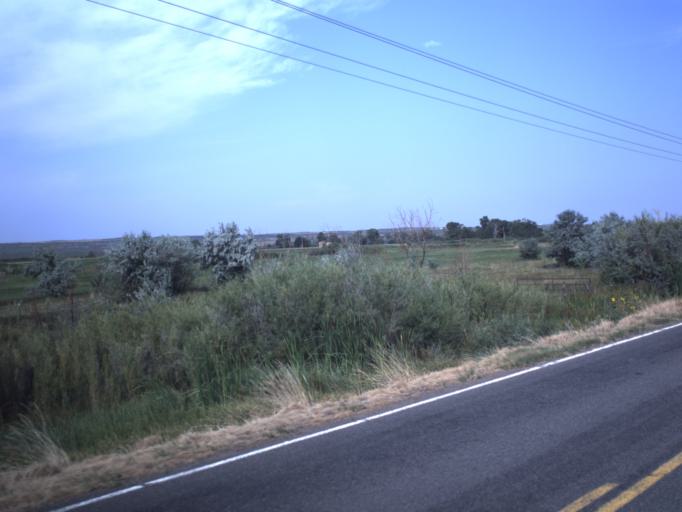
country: US
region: Utah
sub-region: Duchesne County
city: Duchesne
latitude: 40.2890
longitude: -110.2278
